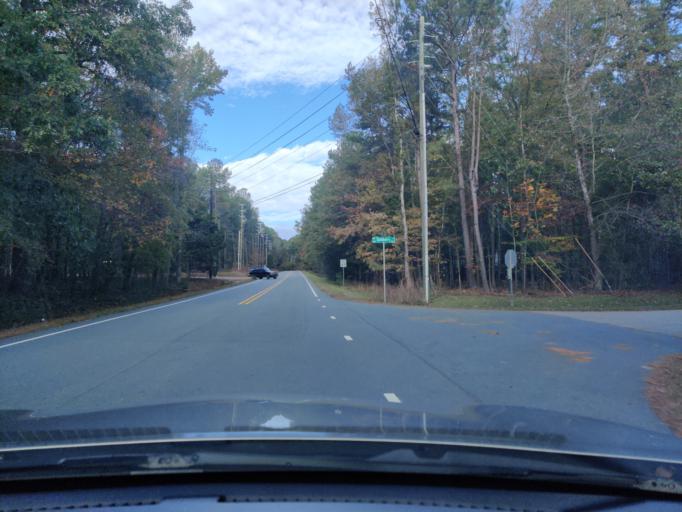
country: US
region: North Carolina
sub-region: Wake County
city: West Raleigh
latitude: 35.9192
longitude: -78.7158
